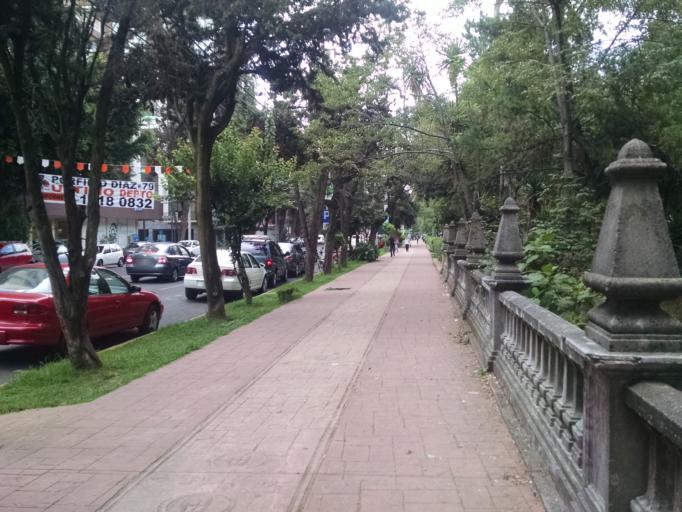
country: MX
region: Mexico City
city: Colonia del Valle
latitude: 19.3791
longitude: -99.1796
